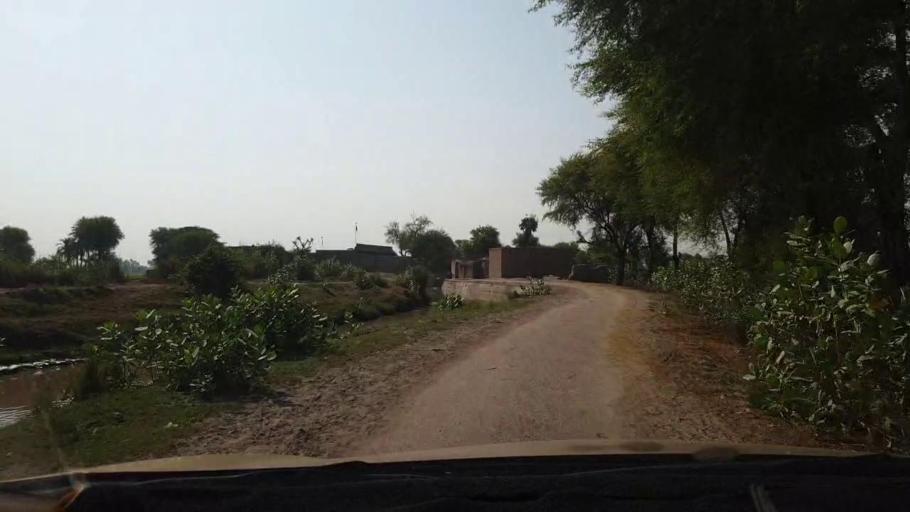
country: PK
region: Sindh
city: Larkana
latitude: 27.6257
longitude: 68.2594
